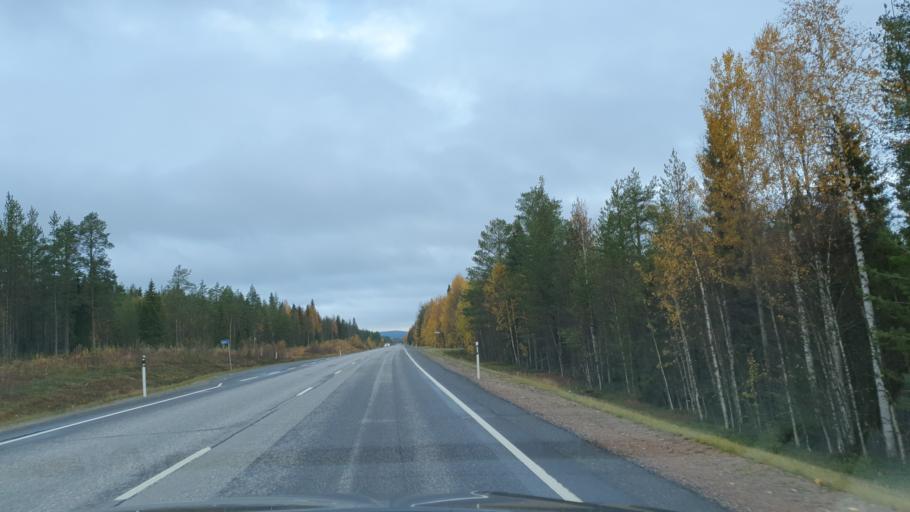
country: FI
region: Lapland
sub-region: Rovaniemi
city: Rovaniemi
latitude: 66.5539
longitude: 25.6503
